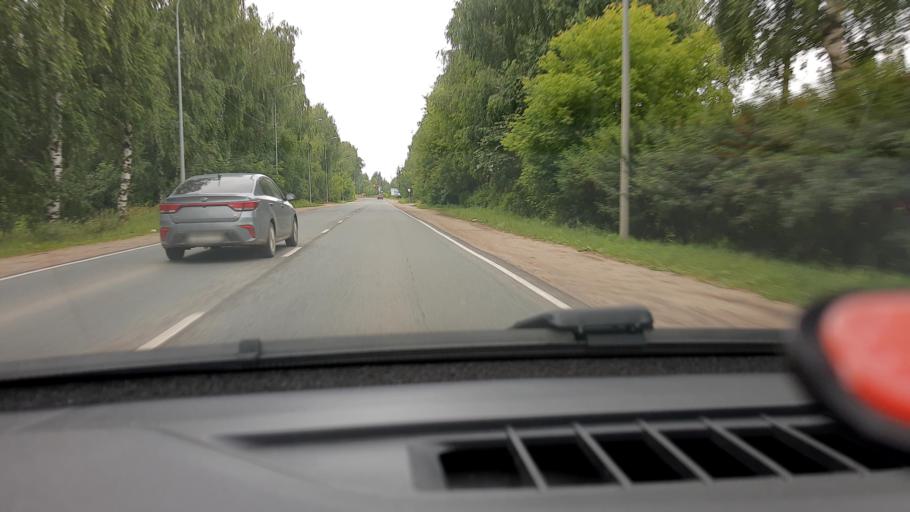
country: RU
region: Nizjnij Novgorod
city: Bor
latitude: 56.3805
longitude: 44.0409
